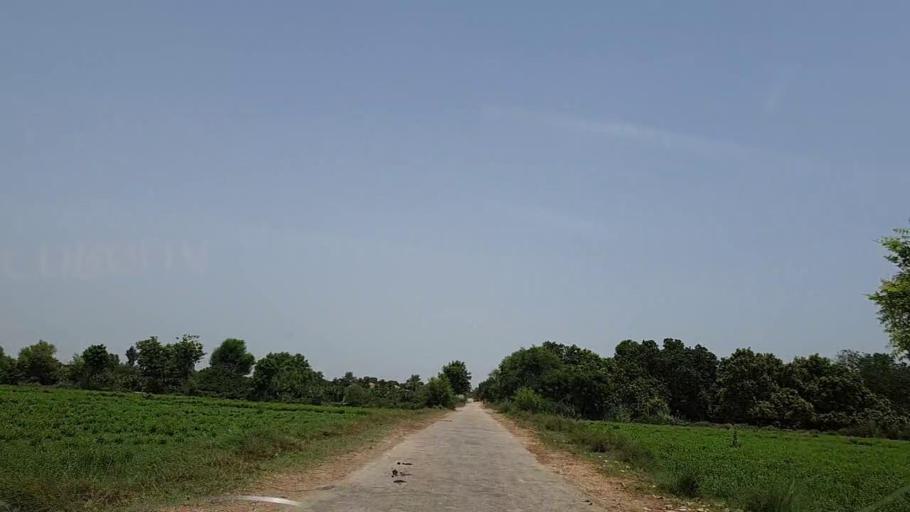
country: PK
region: Sindh
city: Tharu Shah
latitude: 26.9477
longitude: 68.0255
